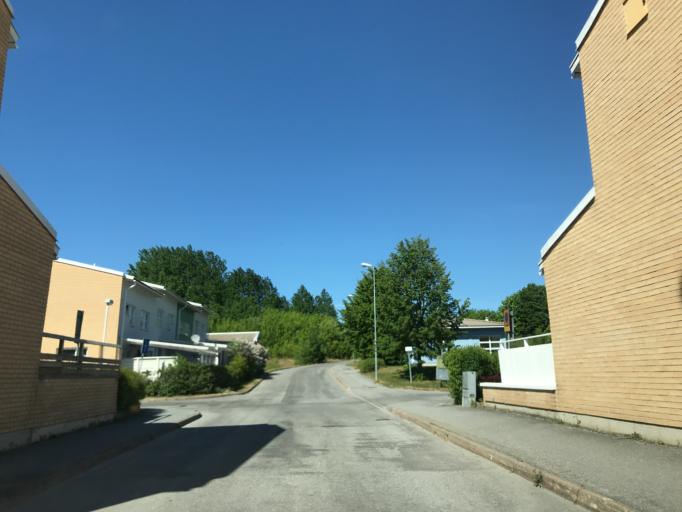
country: SE
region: Stockholm
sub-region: Upplands Vasby Kommun
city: Upplands Vaesby
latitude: 59.4629
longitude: 17.8932
